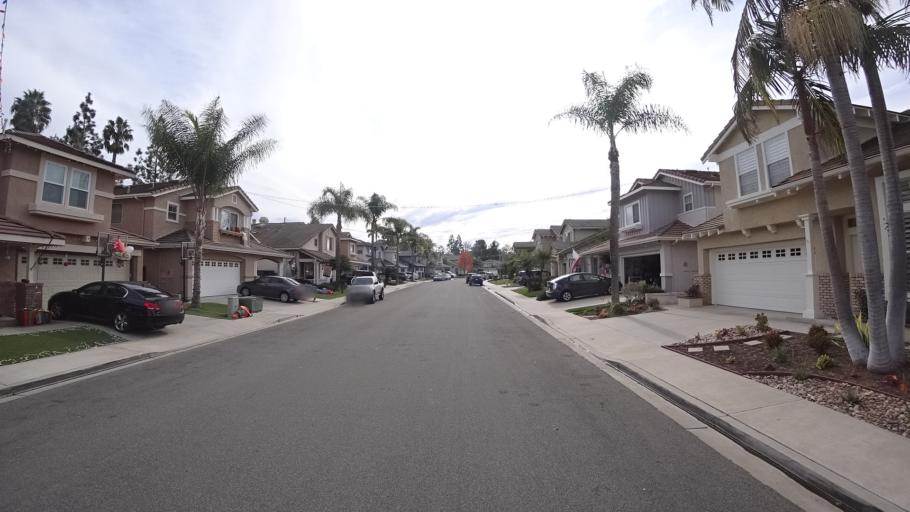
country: US
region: California
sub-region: Orange County
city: Aliso Viejo
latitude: 33.5861
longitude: -117.7403
